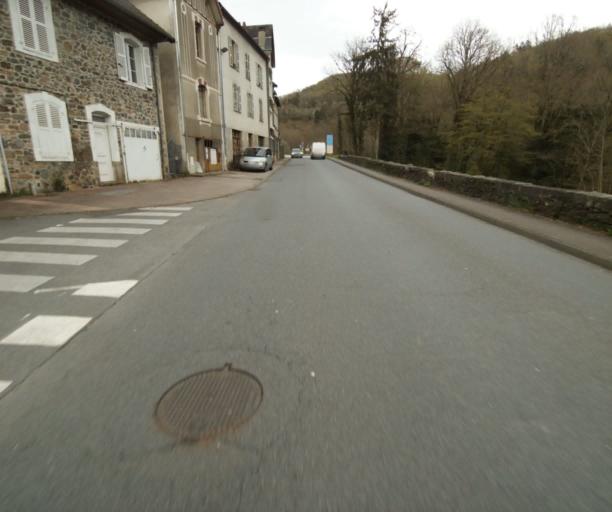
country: FR
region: Limousin
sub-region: Departement de la Correze
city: Laguenne
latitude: 45.2409
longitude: 1.7841
